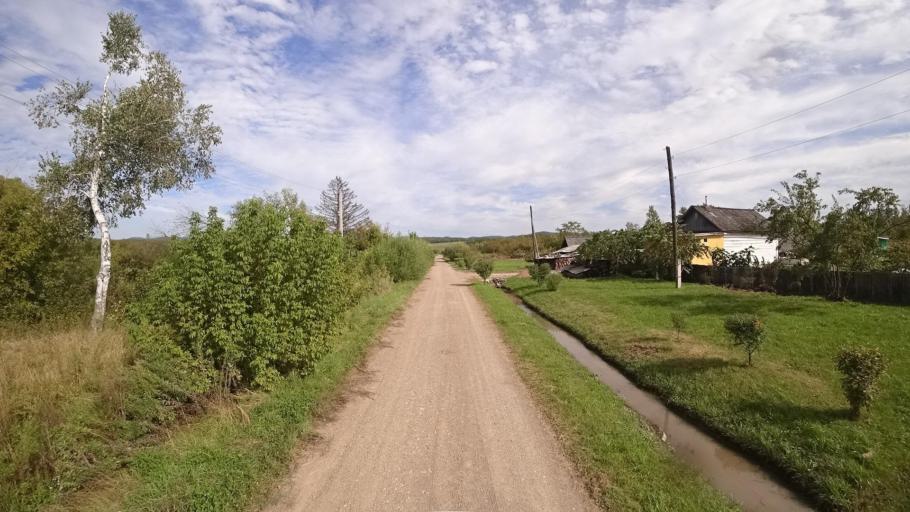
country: RU
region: Primorskiy
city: Dostoyevka
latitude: 44.3276
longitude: 133.4942
